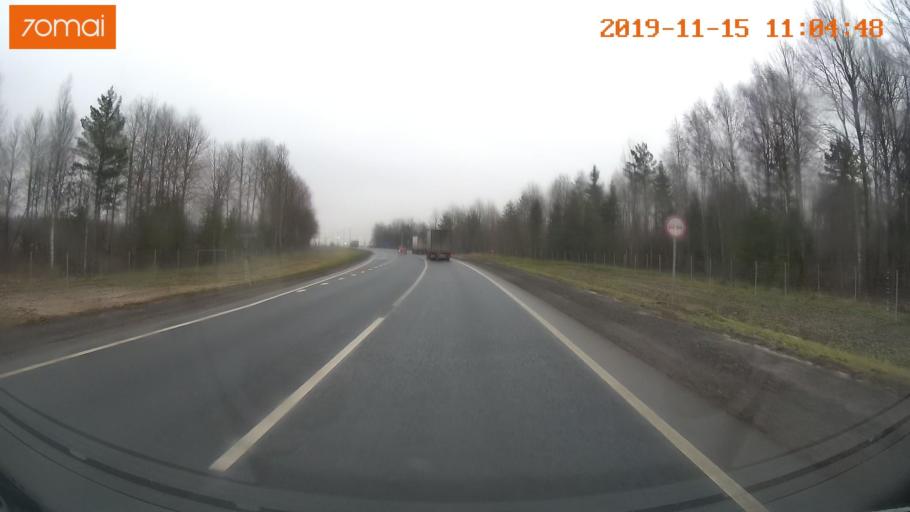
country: RU
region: Vologda
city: Chebsara
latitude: 59.1187
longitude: 38.9911
